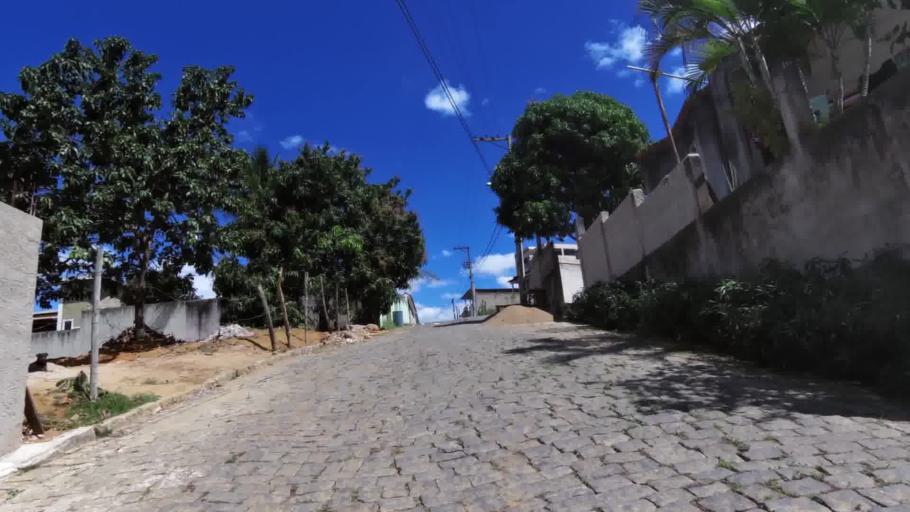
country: BR
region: Espirito Santo
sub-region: Rio Novo Do Sul
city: Rio Novo do Sul
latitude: -20.8659
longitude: -40.9414
